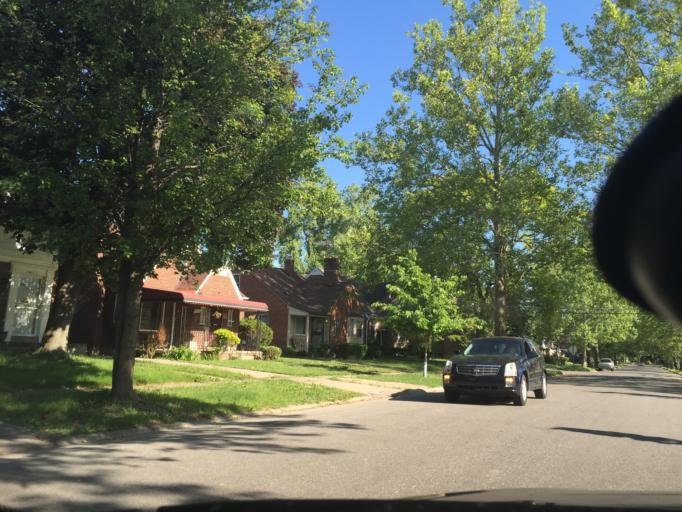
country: US
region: Michigan
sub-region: Oakland County
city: Southfield
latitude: 42.4106
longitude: -83.2252
